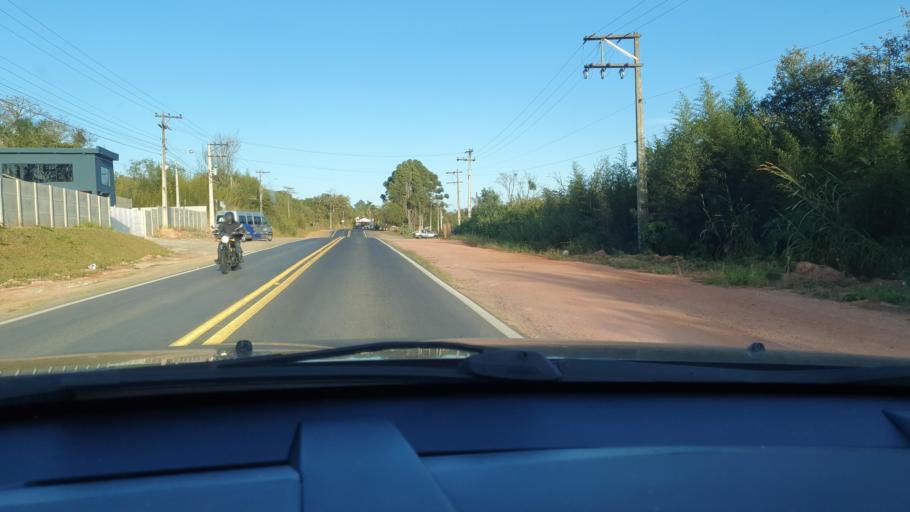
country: BR
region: Sao Paulo
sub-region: Ibiuna
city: Ibiuna
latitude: -23.6761
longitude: -47.3204
